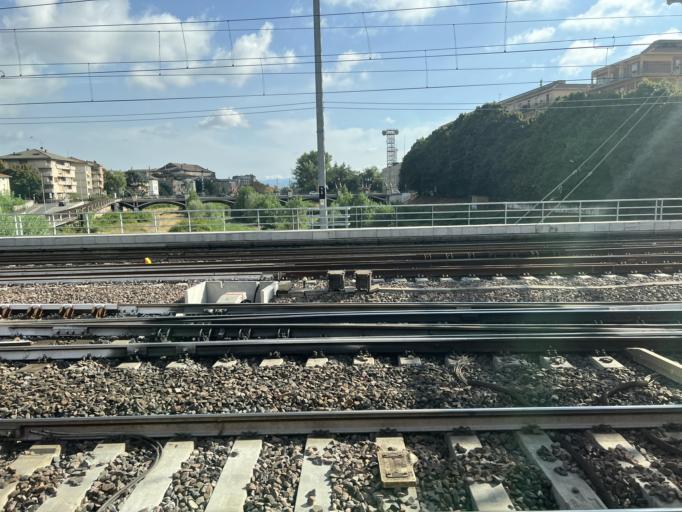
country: IT
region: Emilia-Romagna
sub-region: Provincia di Parma
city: Parma
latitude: 44.8109
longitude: 10.3256
